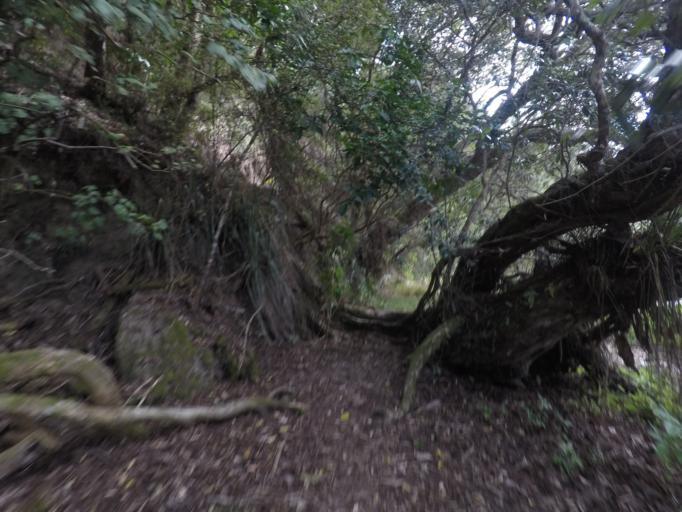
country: NZ
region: Auckland
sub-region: Auckland
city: Rothesay Bay
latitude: -36.6462
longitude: 174.7254
